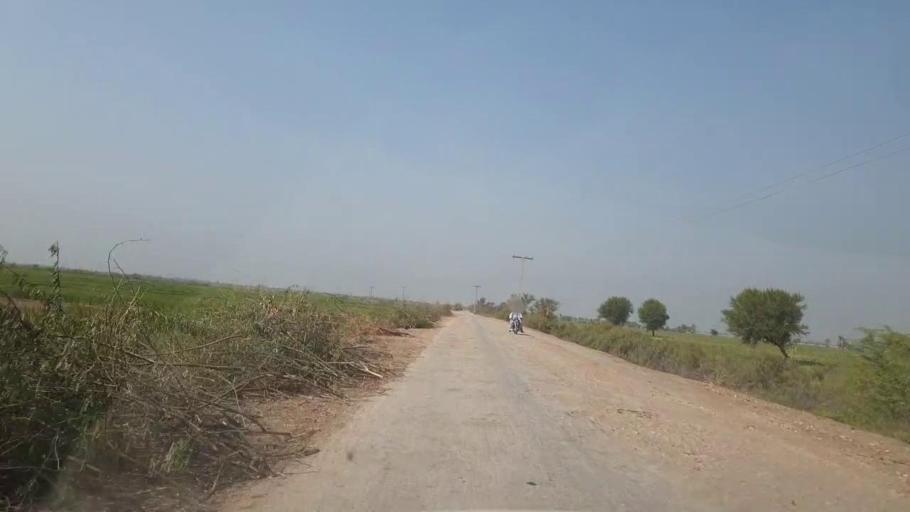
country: PK
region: Sindh
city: Mirpur Khas
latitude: 25.6925
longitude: 69.1494
